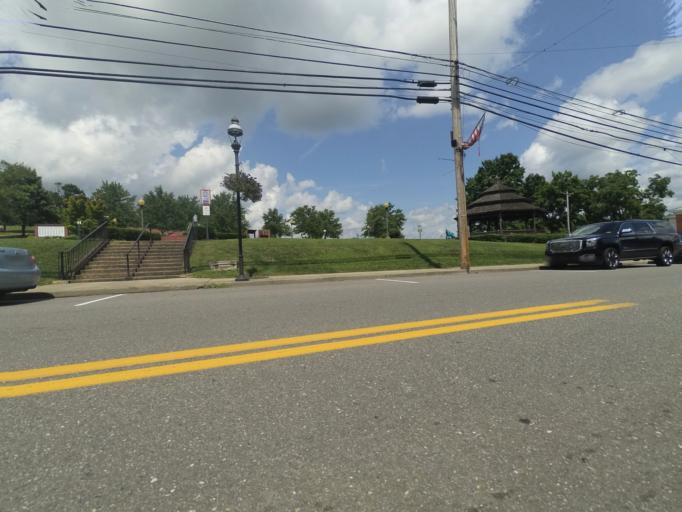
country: US
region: West Virginia
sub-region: Cabell County
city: Barboursville
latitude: 38.4098
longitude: -82.2951
